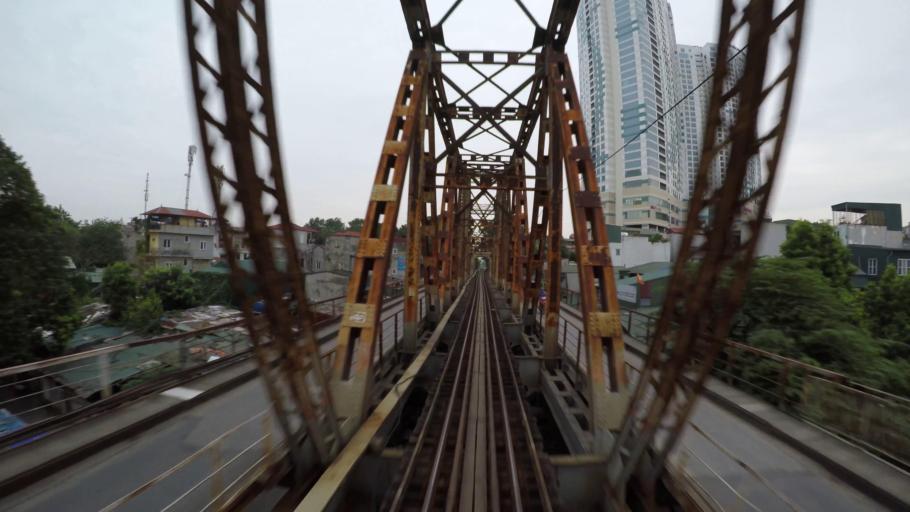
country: VN
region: Ha Noi
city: Hoan Kiem
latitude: 21.0515
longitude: 105.8906
